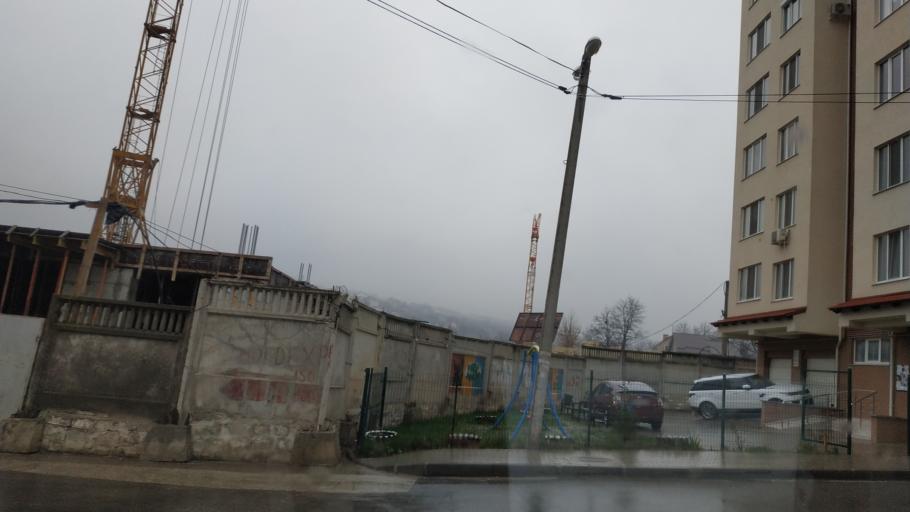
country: MD
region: Chisinau
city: Chisinau
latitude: 47.0201
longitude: 28.7948
